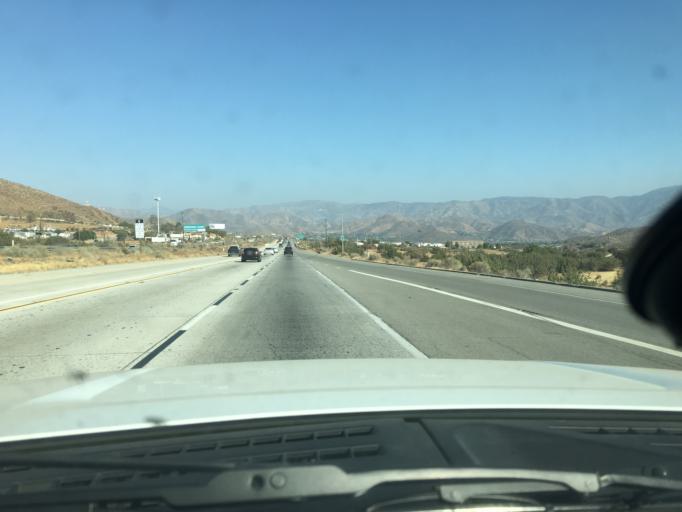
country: US
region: California
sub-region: Los Angeles County
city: Acton
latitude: 34.4987
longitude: -118.2224
